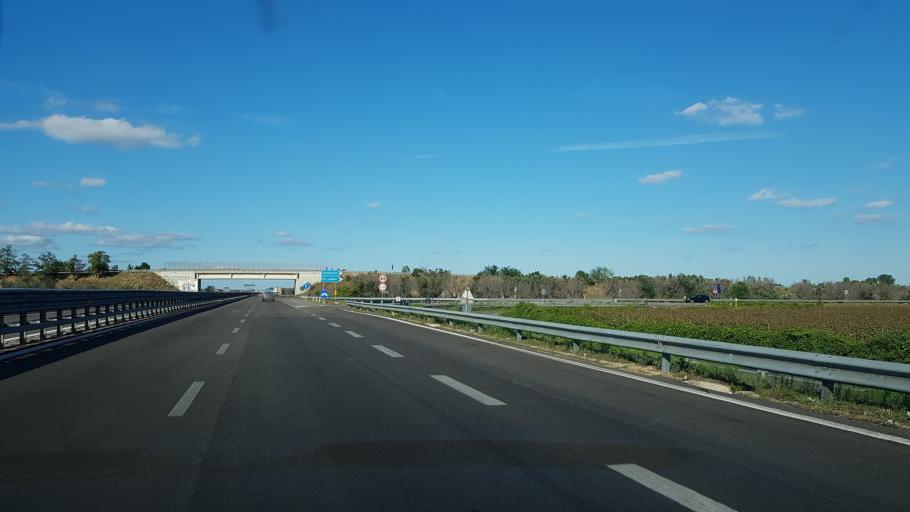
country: IT
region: Apulia
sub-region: Provincia di Lecce
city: Collemeto
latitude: 40.2558
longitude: 18.1180
